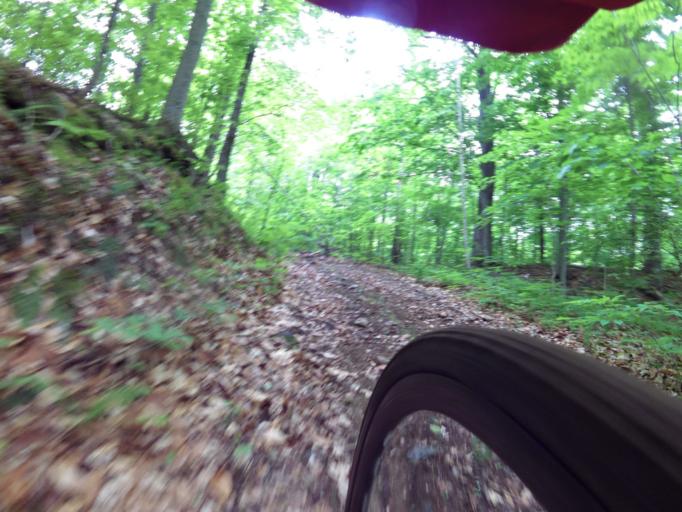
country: CA
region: Ontario
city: Arnprior
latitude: 45.1814
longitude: -76.5326
